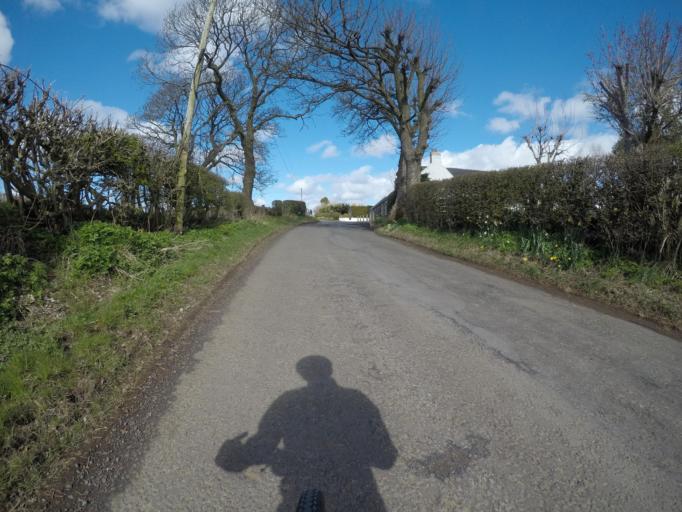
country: GB
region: Scotland
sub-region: East Ayrshire
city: Crosshouse
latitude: 55.6060
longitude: -4.5747
